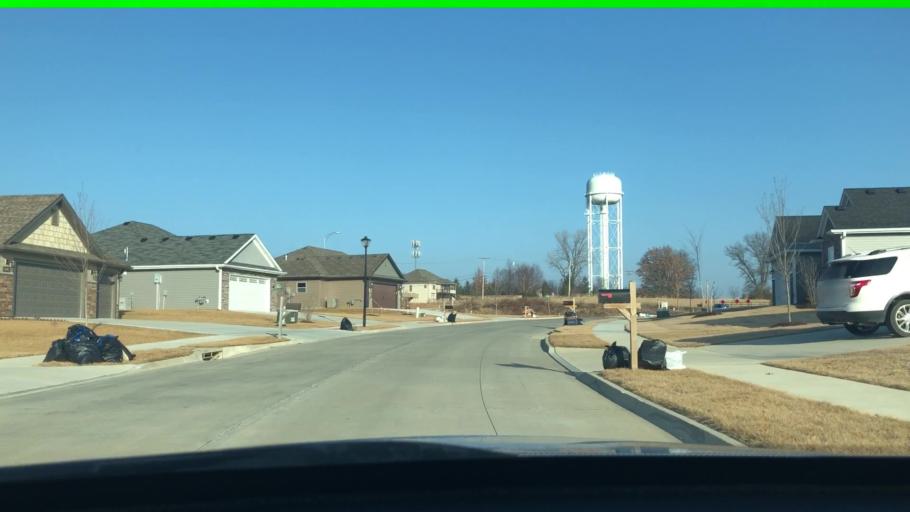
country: US
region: Missouri
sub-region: Boone County
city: Columbia
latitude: 38.8936
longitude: -92.3997
